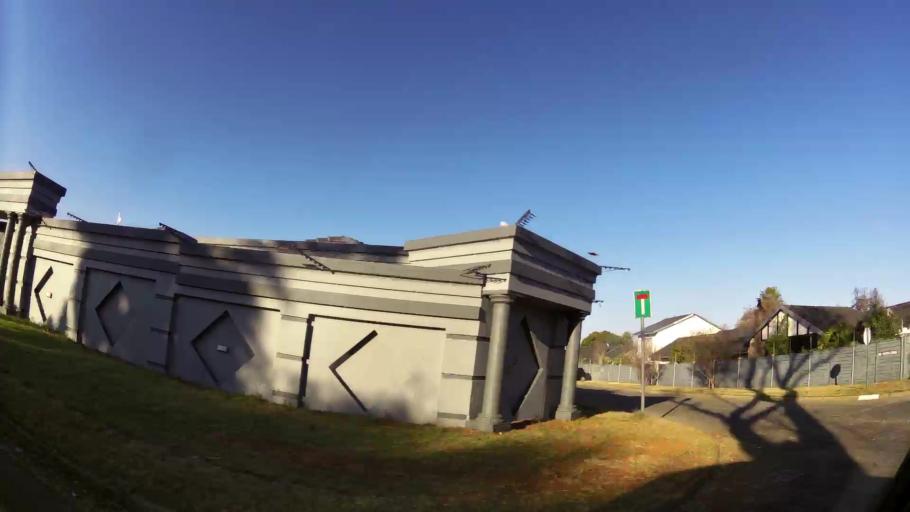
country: ZA
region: Gauteng
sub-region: Ekurhuleni Metropolitan Municipality
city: Germiston
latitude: -26.2854
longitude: 28.1174
